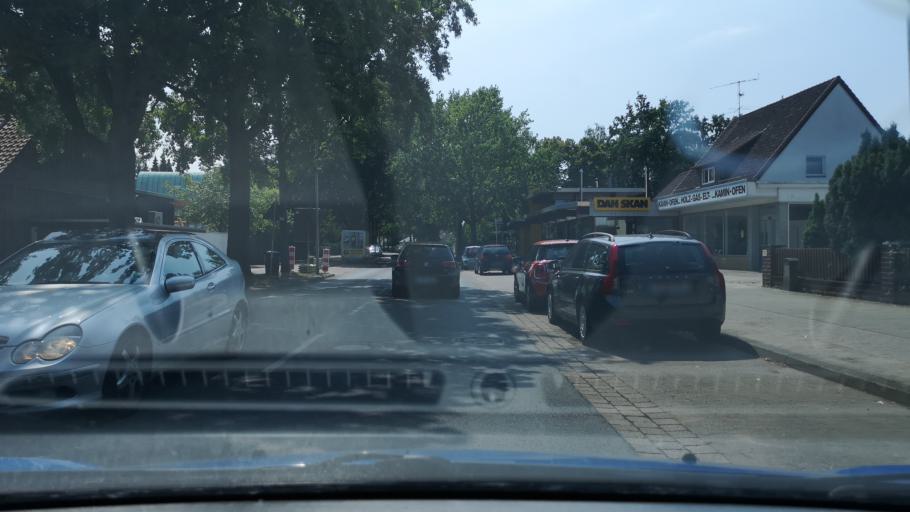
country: DE
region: Lower Saxony
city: Langenhagen
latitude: 52.4200
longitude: 9.7982
